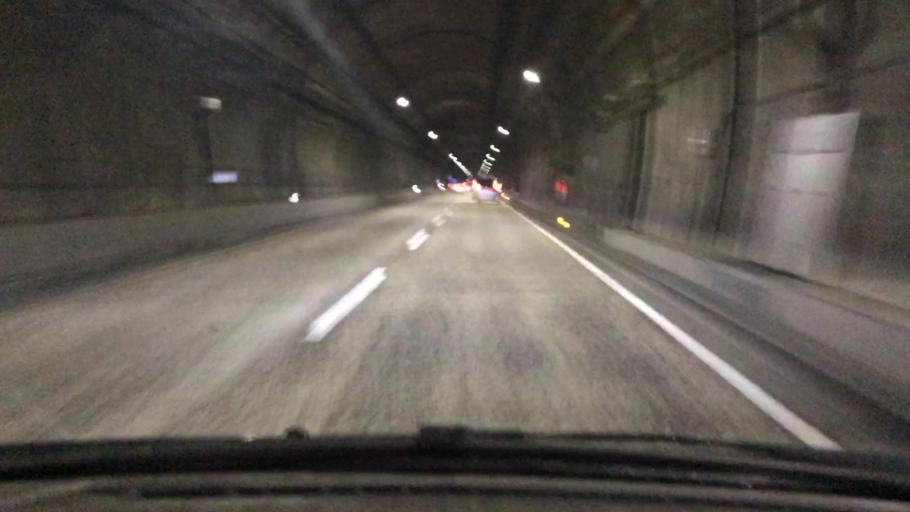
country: JP
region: Hyogo
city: Kobe
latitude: 34.7381
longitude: 135.1739
